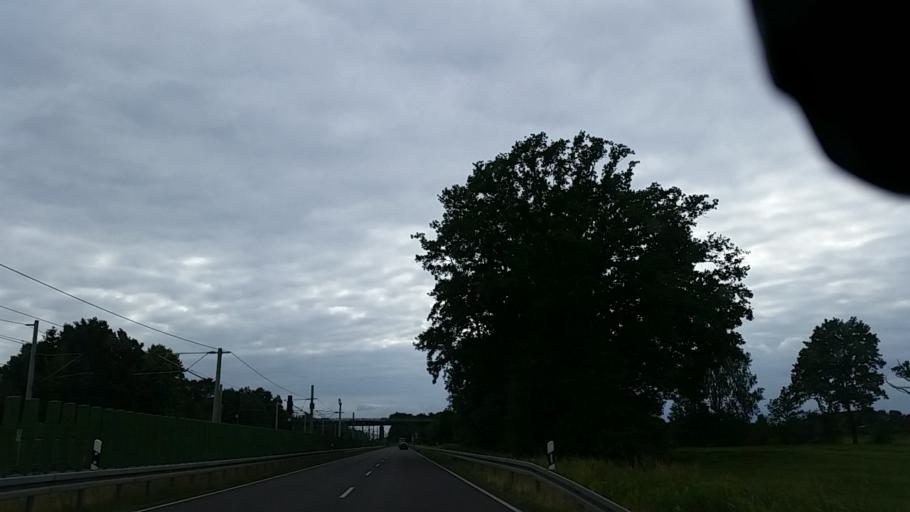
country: DE
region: Lower Saxony
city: Danndorf
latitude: 52.4314
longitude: 10.8747
